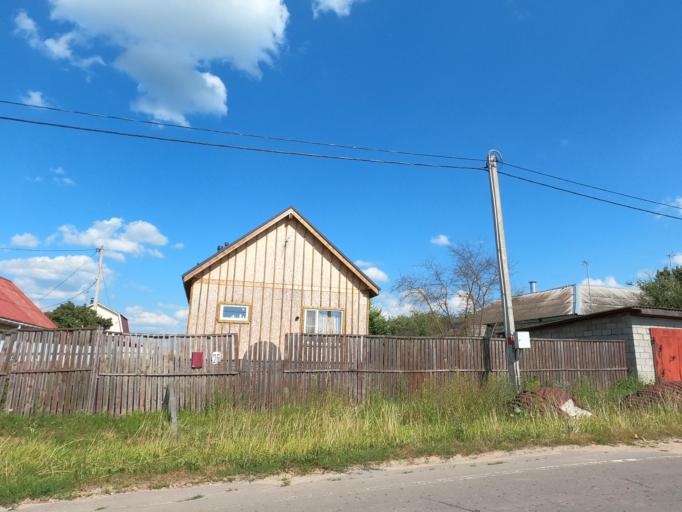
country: RU
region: Moskovskaya
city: Peski
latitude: 55.2276
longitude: 38.7503
